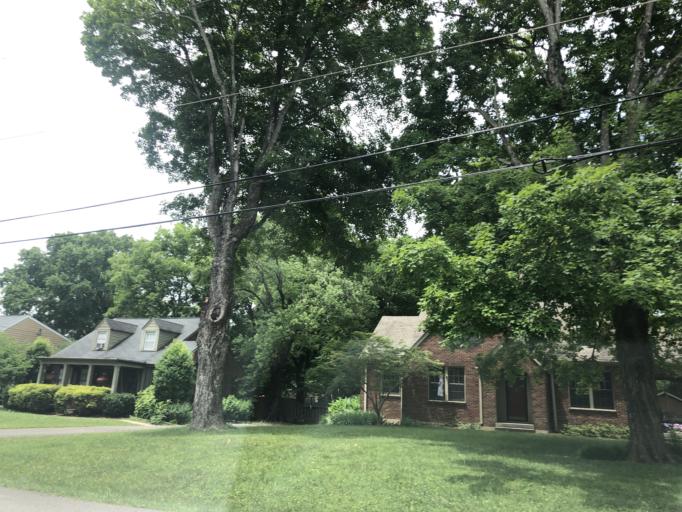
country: US
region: Tennessee
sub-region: Davidson County
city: Oak Hill
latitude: 36.1128
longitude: -86.7848
